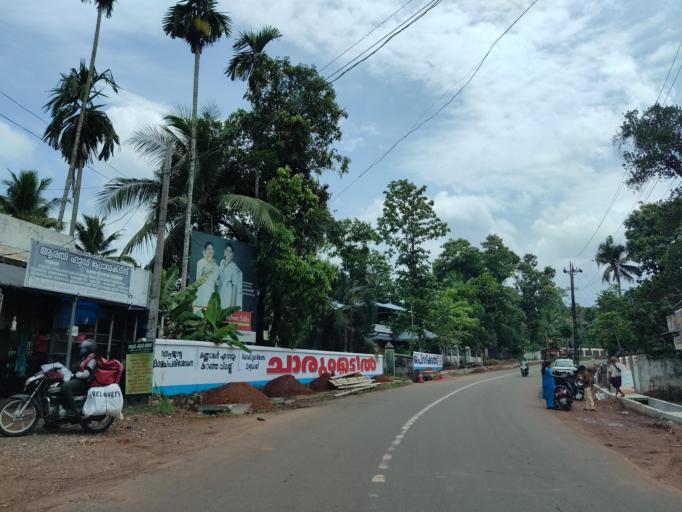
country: IN
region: Kerala
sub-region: Alappuzha
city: Mavelikara
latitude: 9.2296
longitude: 76.6055
